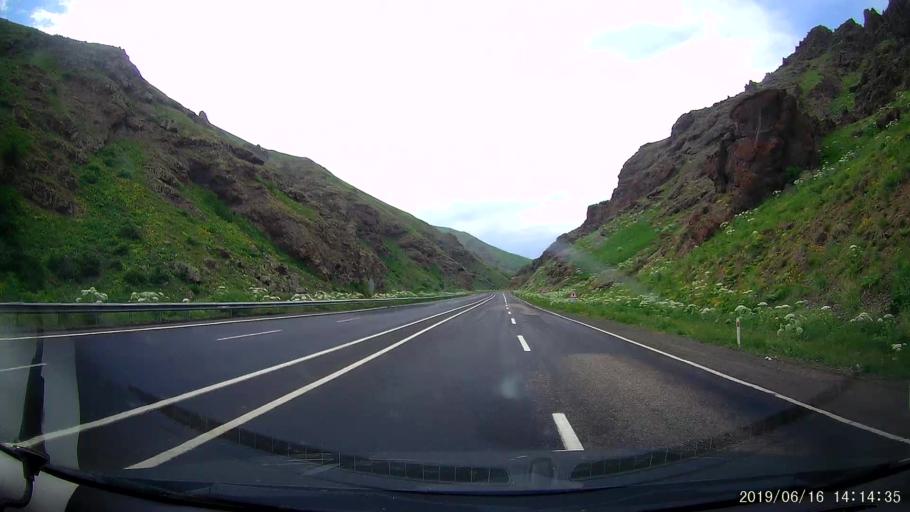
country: TR
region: Agri
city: Tahir
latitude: 39.7963
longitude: 42.4944
